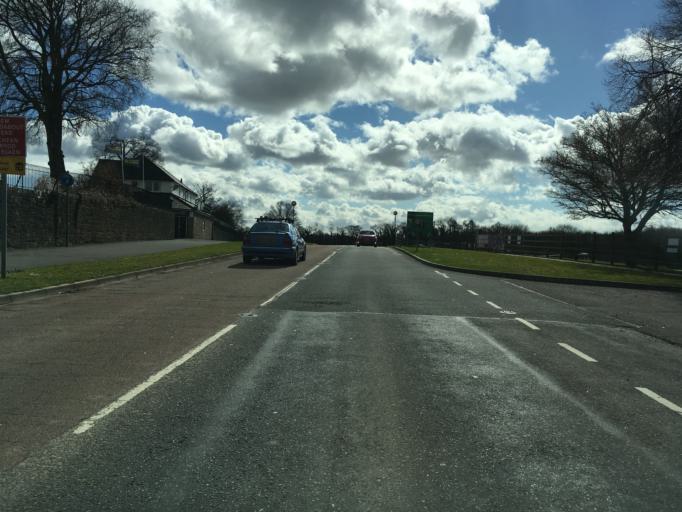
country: GB
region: Wales
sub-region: Monmouthshire
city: Chepstow
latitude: 51.6516
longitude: -2.6923
